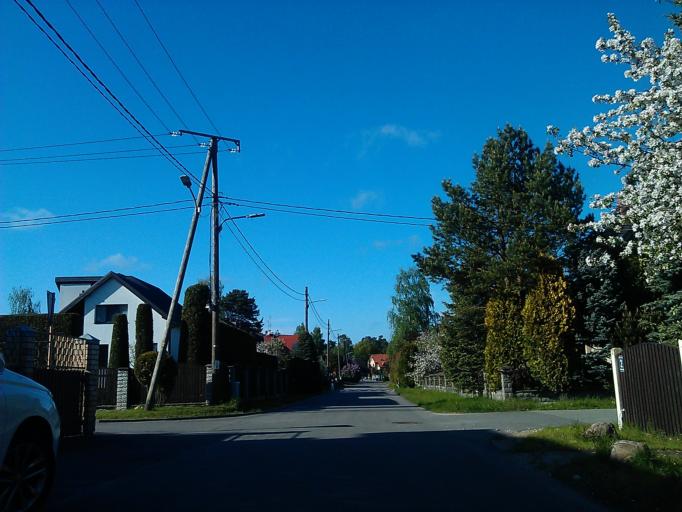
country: LV
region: Riga
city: Bergi
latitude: 57.0121
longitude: 24.2695
